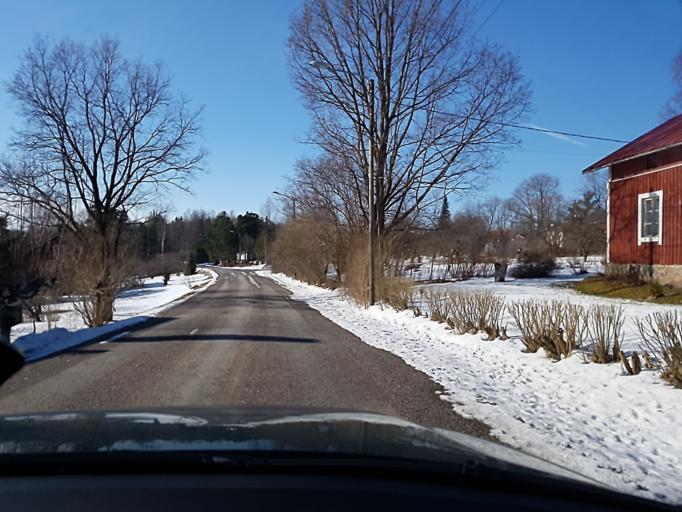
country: FI
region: Uusimaa
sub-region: Helsinki
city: Lohja
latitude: 60.1780
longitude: 23.9791
